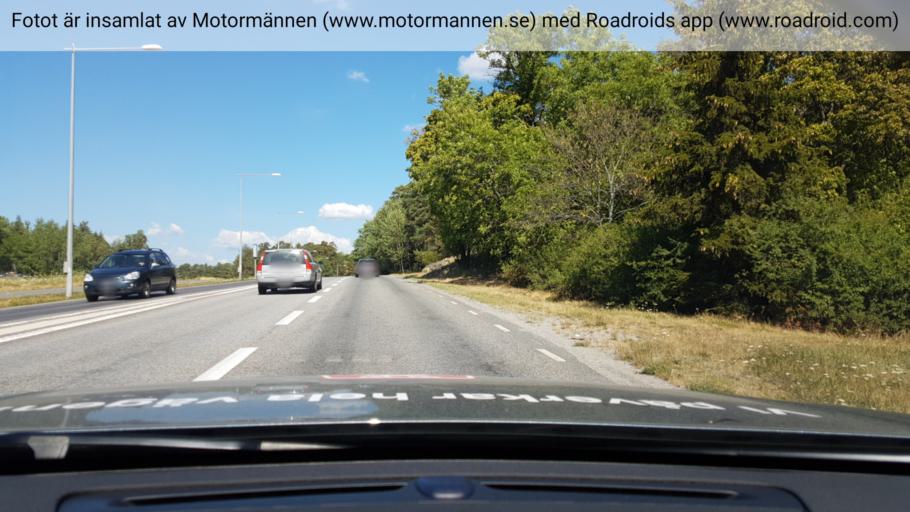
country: SE
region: Stockholm
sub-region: Ekero Kommun
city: Ekeroe
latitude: 59.3103
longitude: 17.8610
